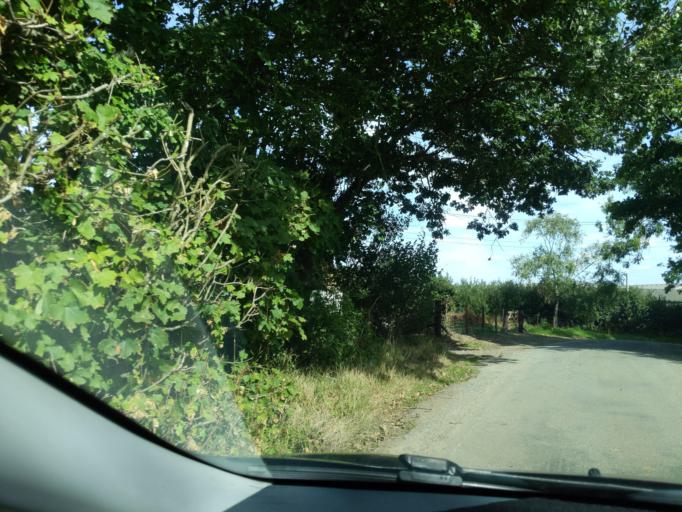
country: GB
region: England
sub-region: Cornwall
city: Torpoint
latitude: 50.3588
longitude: -4.2291
